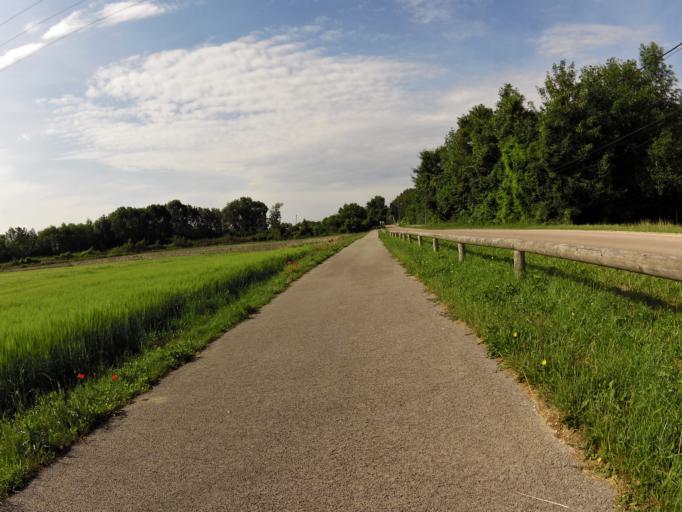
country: FR
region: Champagne-Ardenne
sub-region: Departement de l'Aube
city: Saint-Julien-les-Villas
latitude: 48.2727
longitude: 4.1112
